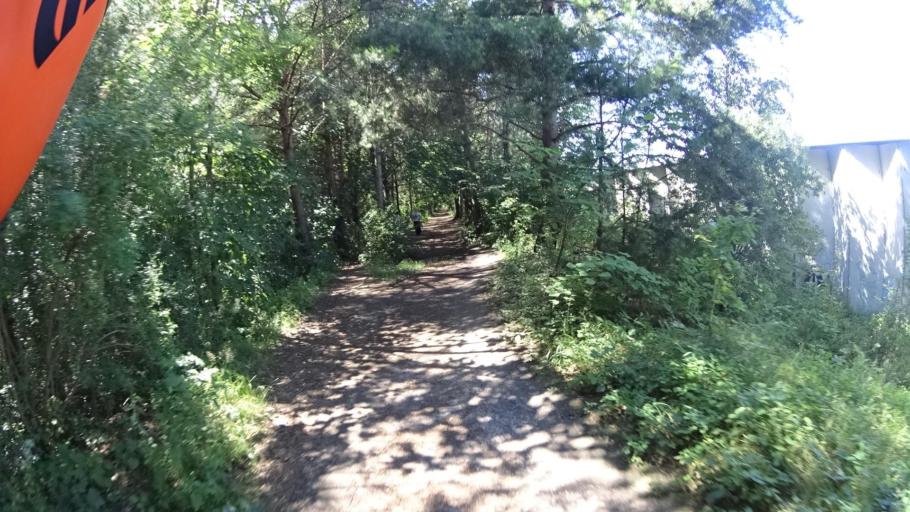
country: PL
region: Masovian Voivodeship
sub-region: Warszawa
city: Kabaty
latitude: 52.1252
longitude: 21.0636
